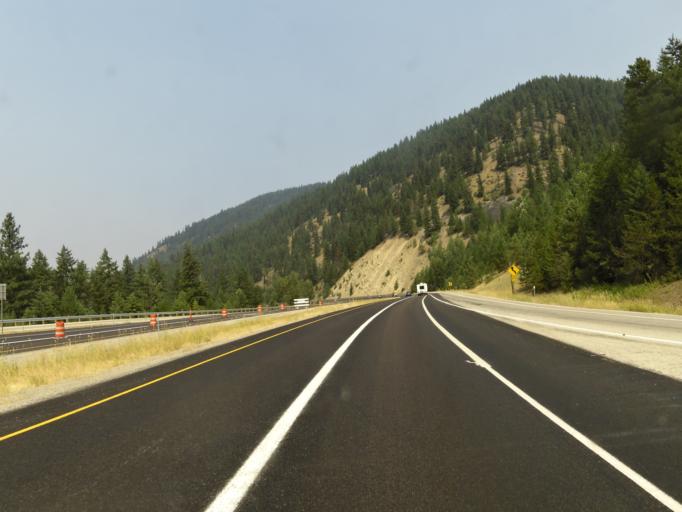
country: US
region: Montana
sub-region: Sanders County
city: Thompson Falls
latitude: 47.3241
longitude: -115.2494
